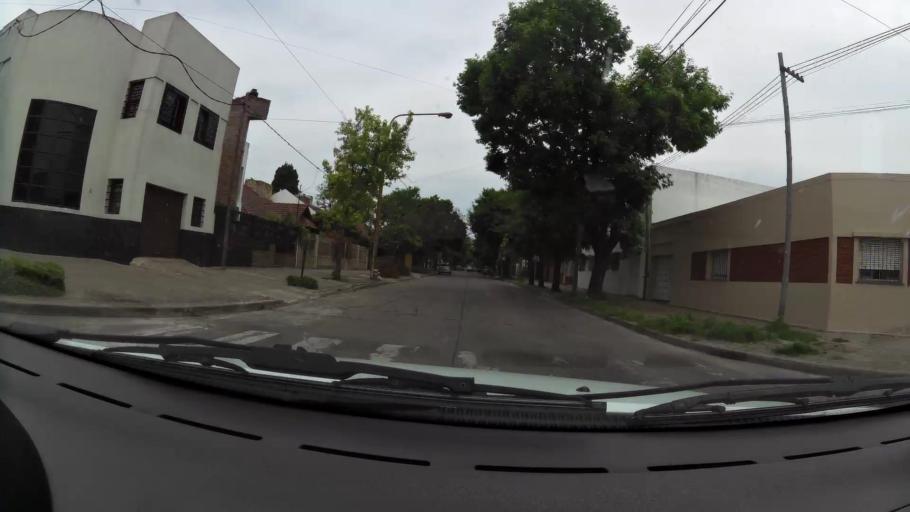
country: AR
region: Buenos Aires
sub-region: Partido de La Plata
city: La Plata
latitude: -34.9392
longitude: -57.9674
